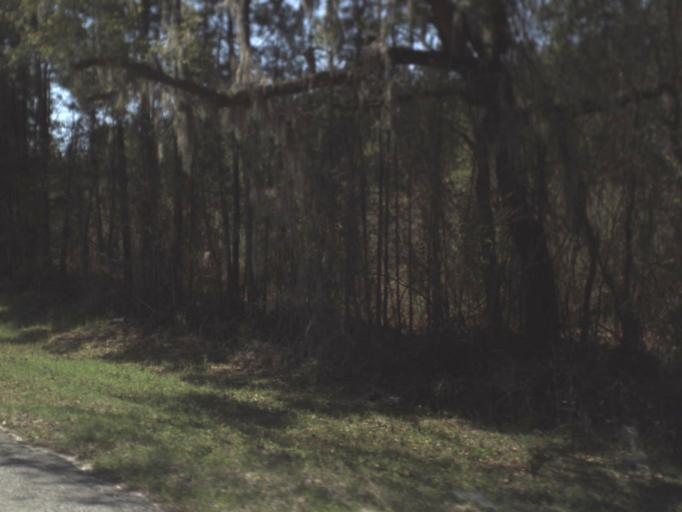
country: US
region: Florida
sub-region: Jefferson County
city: Monticello
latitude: 30.3924
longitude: -84.0132
